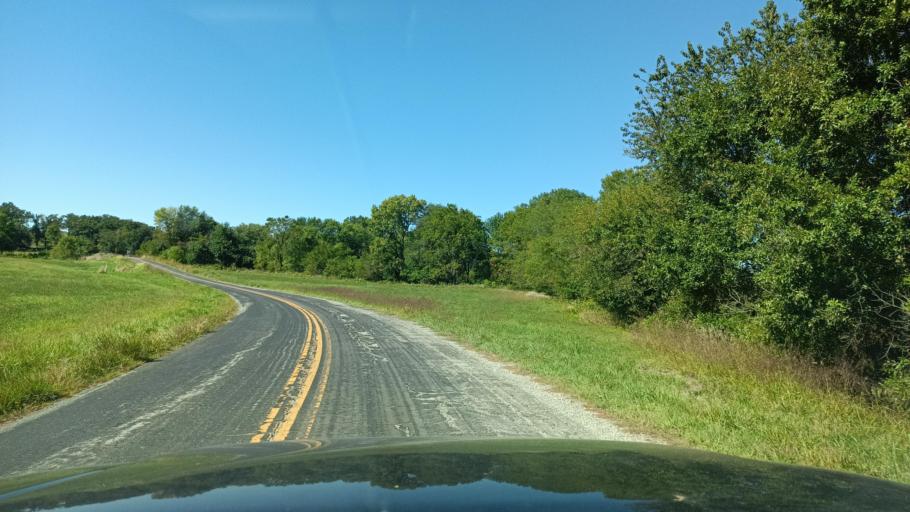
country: US
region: Missouri
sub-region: Scotland County
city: Memphis
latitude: 40.3502
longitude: -92.3215
